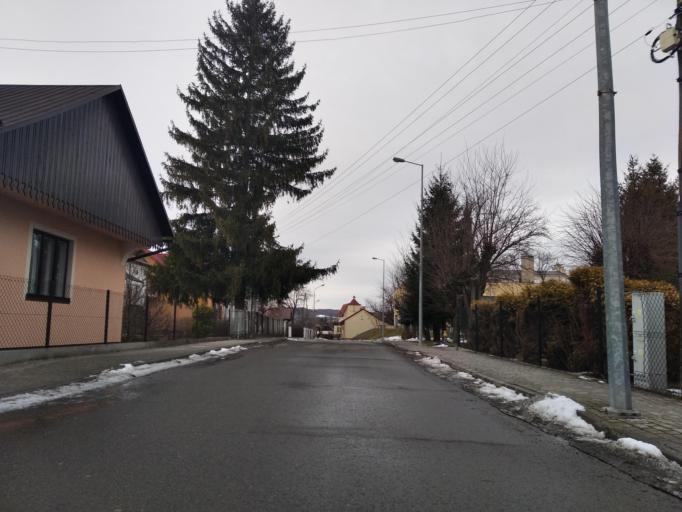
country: PL
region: Subcarpathian Voivodeship
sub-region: Powiat przemyski
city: Dubiecko
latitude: 49.8238
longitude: 22.3927
